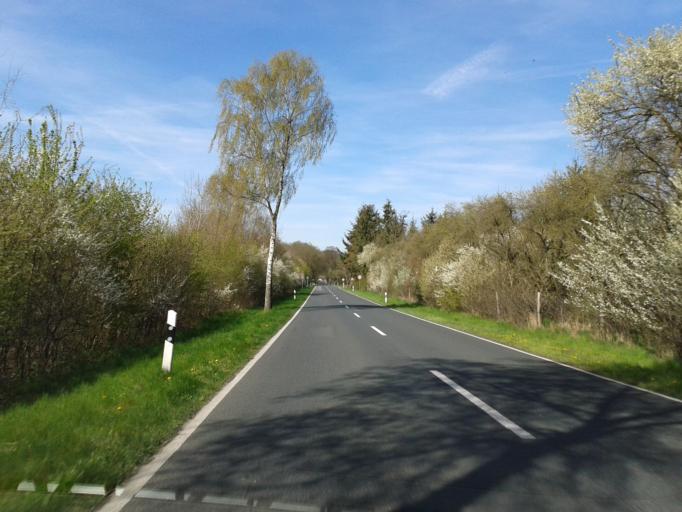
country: DE
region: Lower Saxony
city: Clenze
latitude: 52.9365
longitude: 10.9718
